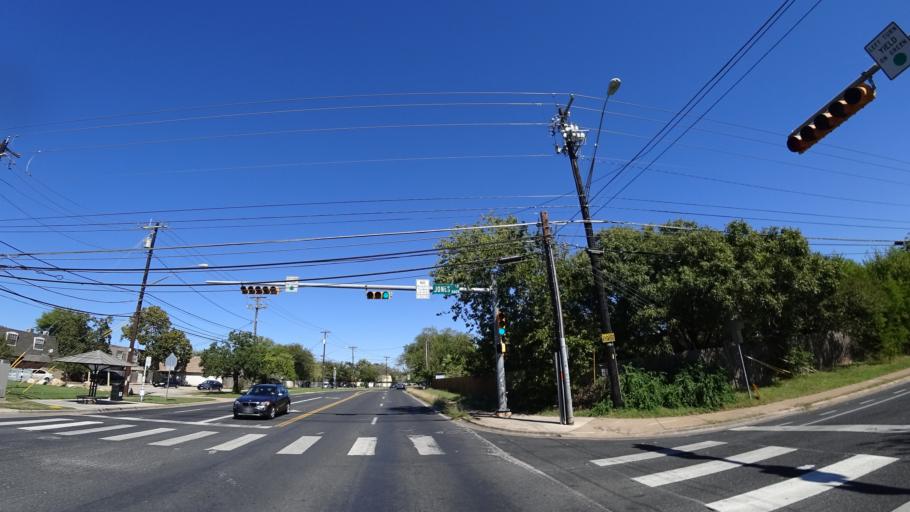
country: US
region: Texas
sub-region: Travis County
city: Rollingwood
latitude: 30.2255
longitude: -97.8038
